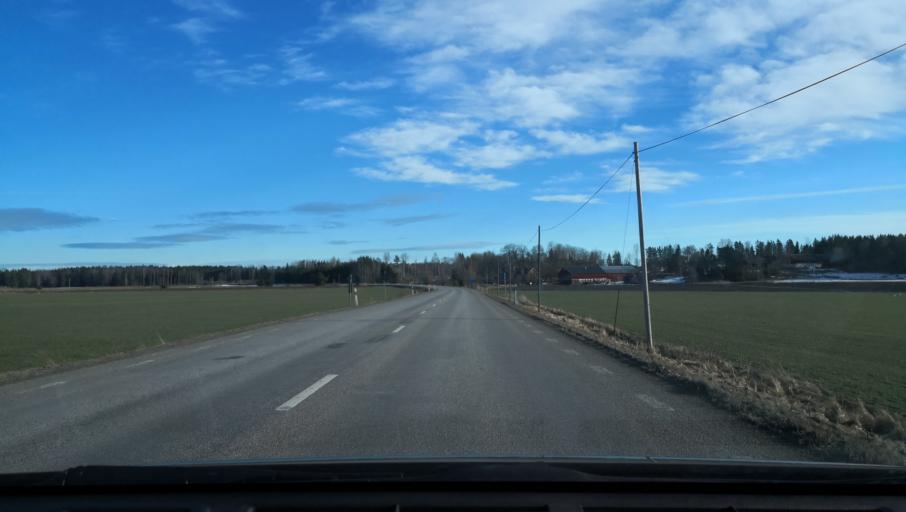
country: SE
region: Uppsala
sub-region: Osthammars Kommun
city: Osterbybruk
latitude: 60.1647
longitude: 17.9782
